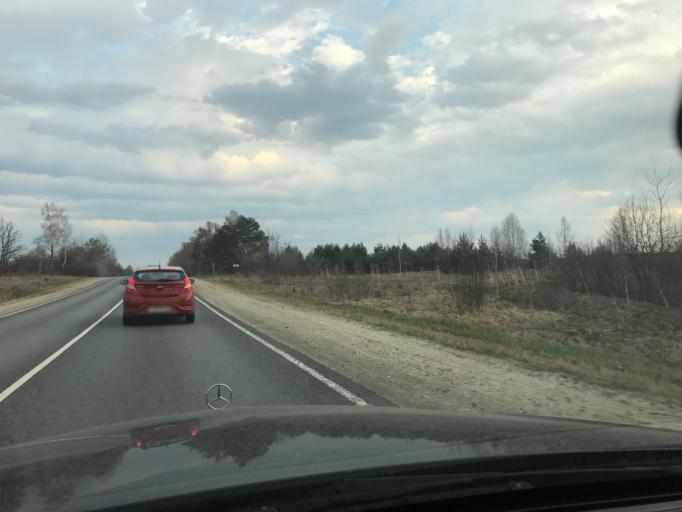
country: RU
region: Vladimir
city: Murom
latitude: 55.6436
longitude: 41.8418
